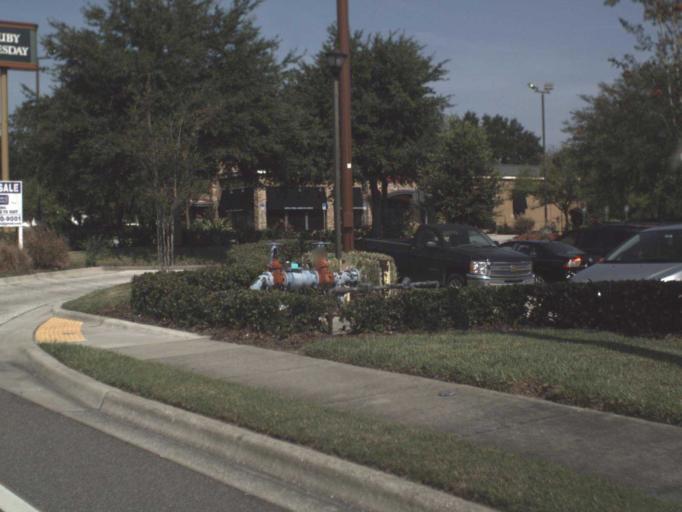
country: US
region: Florida
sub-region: Hillsborough County
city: Valrico
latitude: 27.9380
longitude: -82.2570
